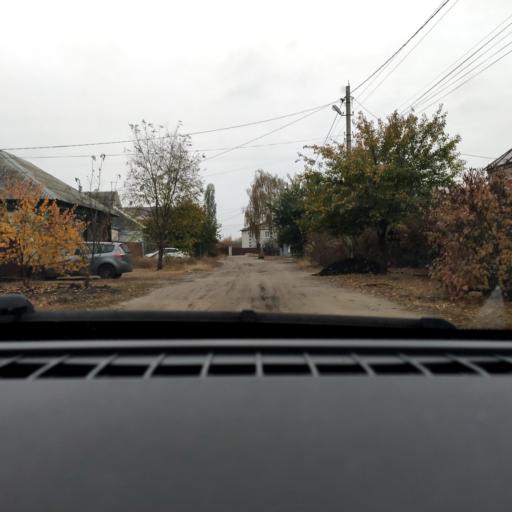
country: RU
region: Voronezj
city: Somovo
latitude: 51.7337
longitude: 39.2863
